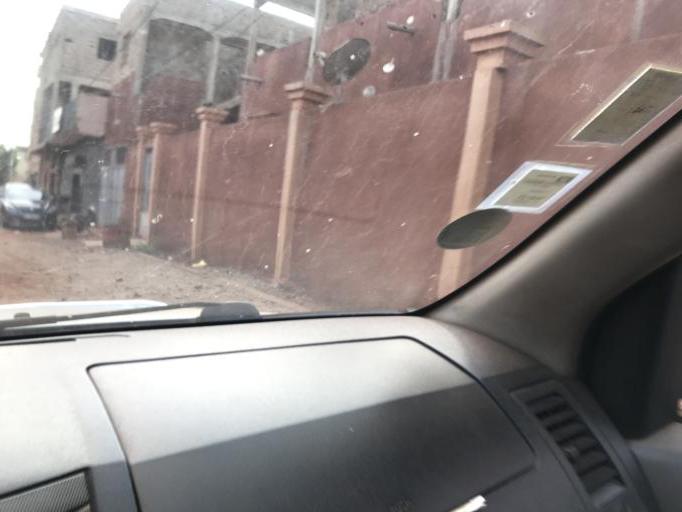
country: ML
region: Bamako
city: Bamako
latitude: 12.5803
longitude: -8.0059
